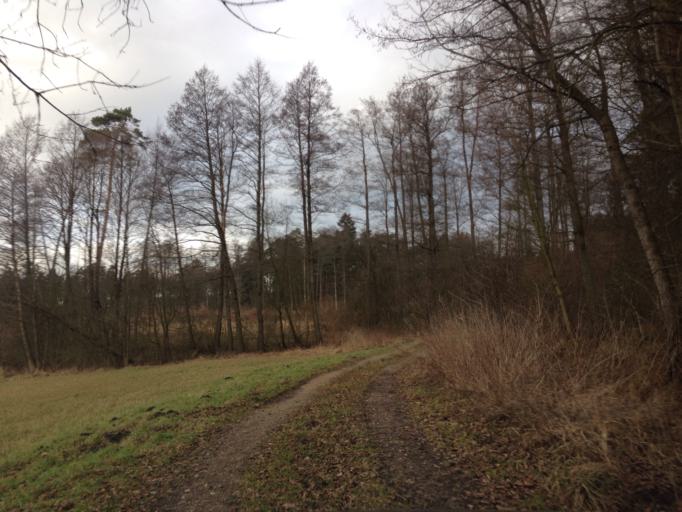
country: PL
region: Kujawsko-Pomorskie
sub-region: Powiat brodnicki
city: Gorzno
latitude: 53.2392
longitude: 19.6544
